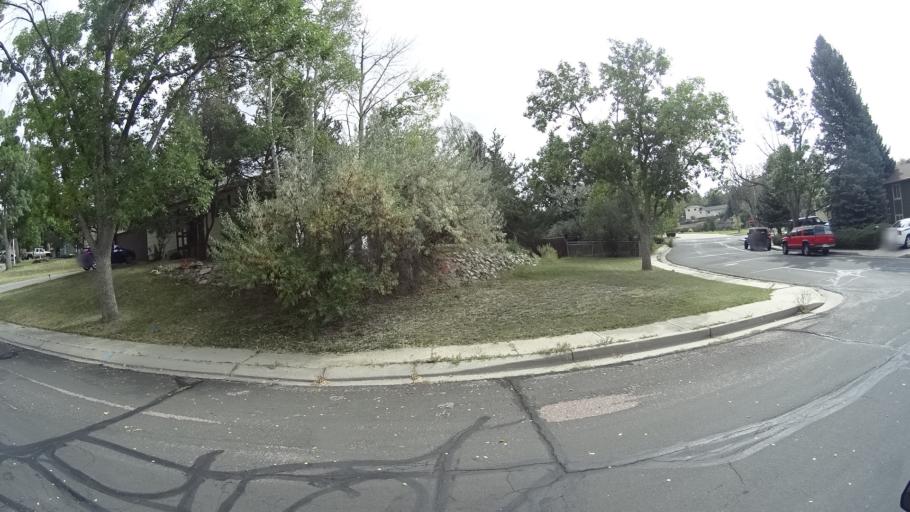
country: US
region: Colorado
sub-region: El Paso County
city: Cimarron Hills
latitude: 38.8806
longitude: -104.7405
